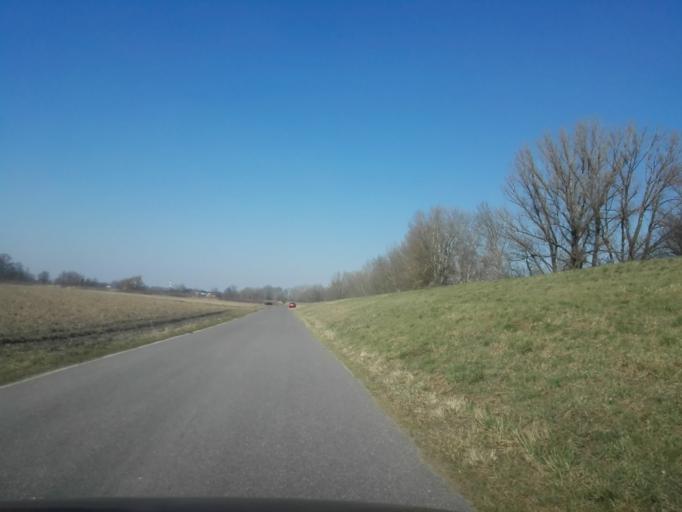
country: PL
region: Masovian Voivodeship
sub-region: Powiat piaseczynski
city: Konstancin-Jeziorna
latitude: 52.1320
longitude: 21.1677
